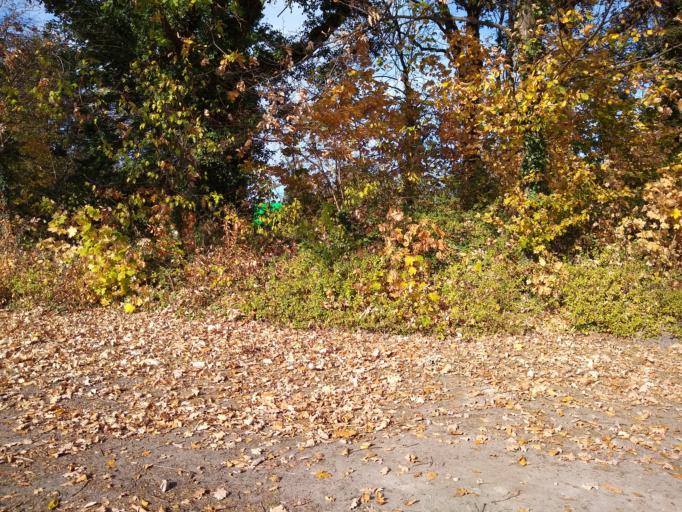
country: DE
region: Lower Saxony
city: Oldenburg
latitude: 53.1597
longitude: 8.1728
